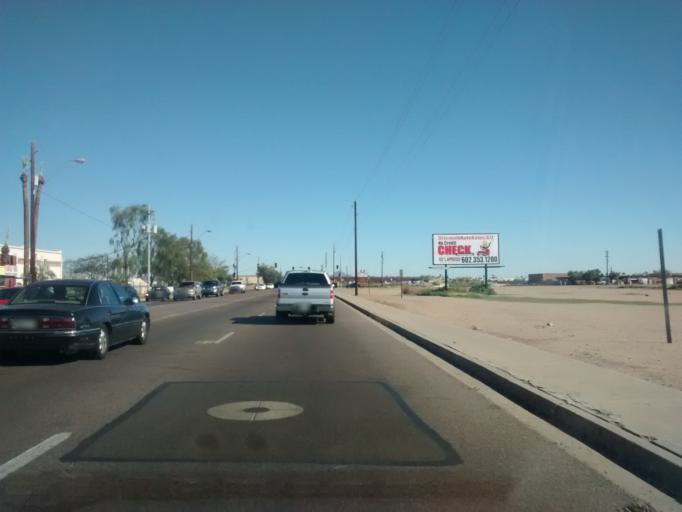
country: US
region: Arizona
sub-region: Maricopa County
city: Glendale
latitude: 33.5241
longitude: -112.1796
